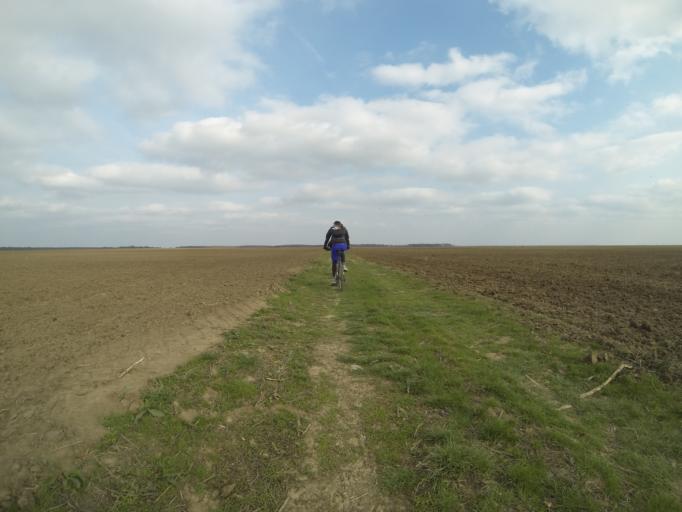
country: RO
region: Dolj
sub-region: Comuna Bucovat
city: Bucovat
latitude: 44.2484
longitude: 23.7084
